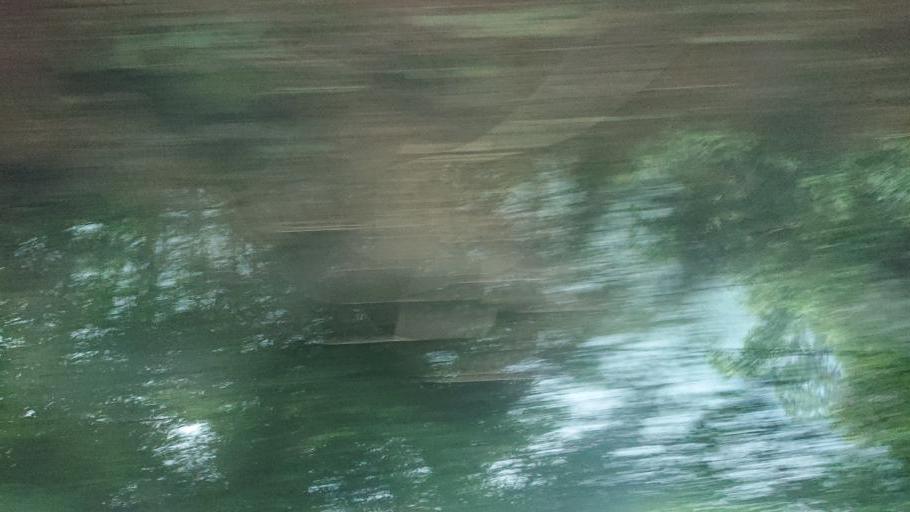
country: TW
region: Taiwan
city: Lugu
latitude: 23.5946
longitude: 120.7173
